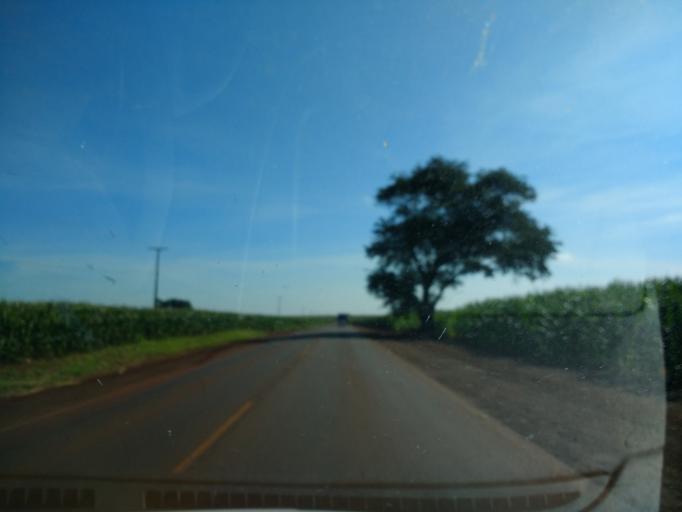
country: BR
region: Parana
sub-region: Palotina
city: Palotina
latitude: -24.3884
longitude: -53.5404
